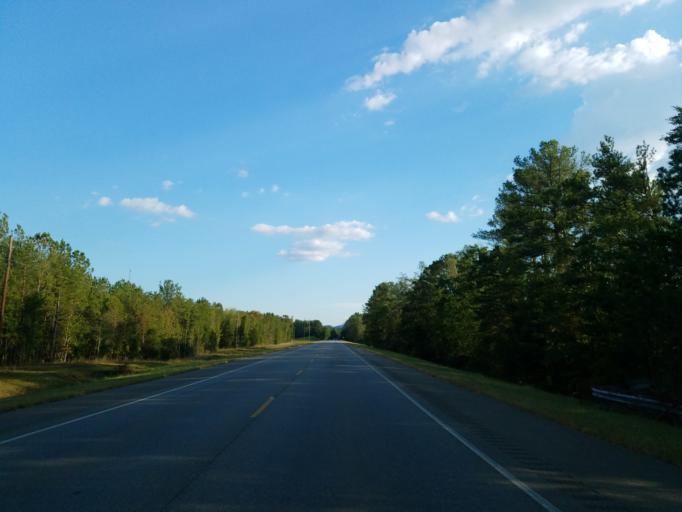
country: US
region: Georgia
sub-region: Murray County
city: Chatsworth
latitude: 34.6480
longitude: -84.7173
